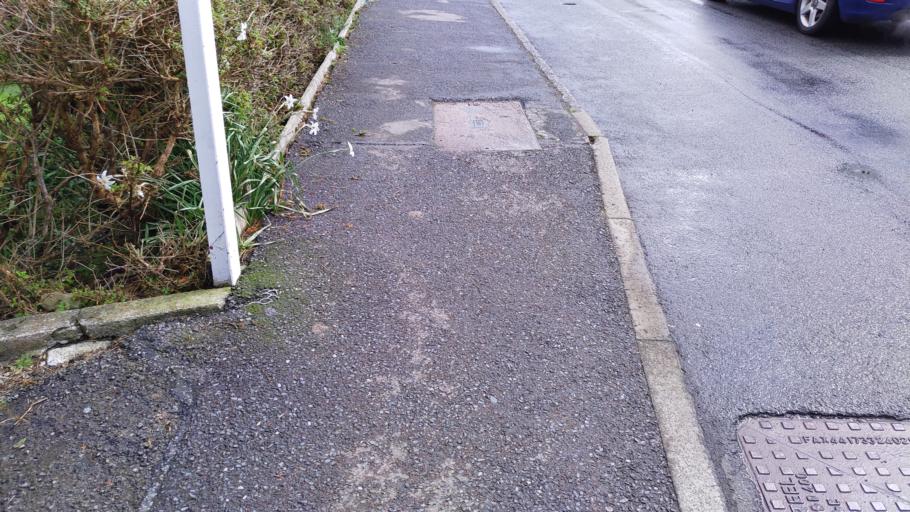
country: GB
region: Scotland
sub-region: Shetland Islands
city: Shetland
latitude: 60.1515
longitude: -1.1354
